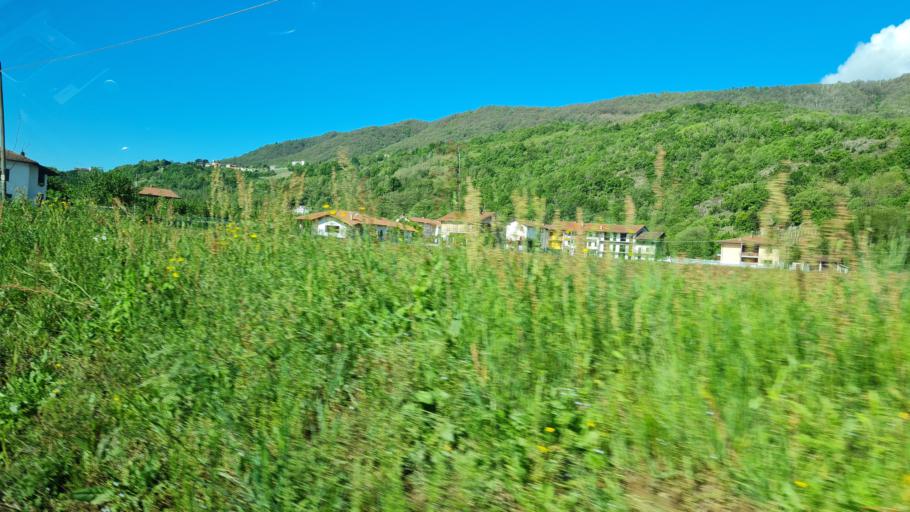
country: IT
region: Piedmont
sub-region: Provincia di Torino
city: Loranze
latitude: 45.4475
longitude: 7.8141
